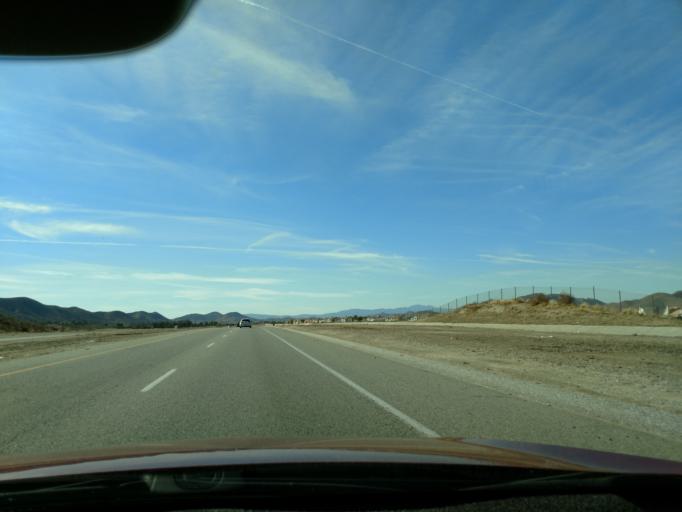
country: US
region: California
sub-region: Riverside County
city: Hemet
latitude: 33.7122
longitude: -117.0118
